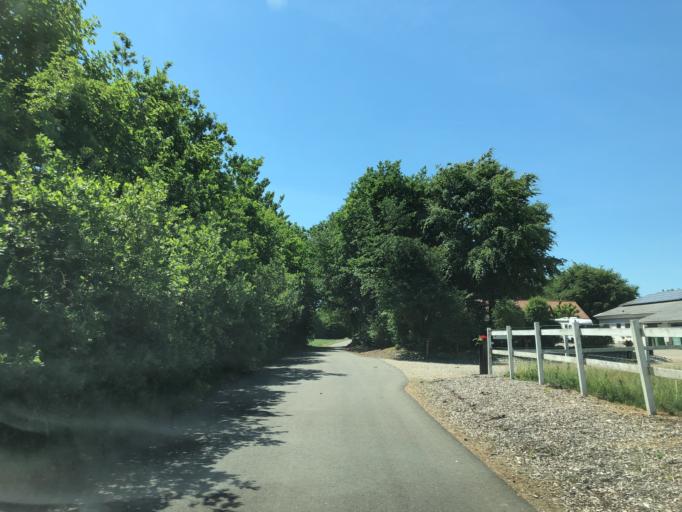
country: DK
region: Central Jutland
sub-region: Struer Kommune
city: Struer
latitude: 56.4316
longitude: 8.4423
